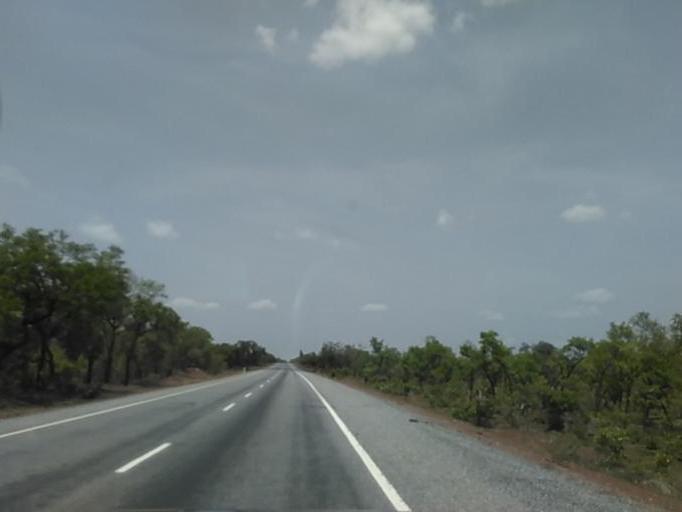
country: GH
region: Northern
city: Tamale
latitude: 9.1457
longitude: -1.3697
